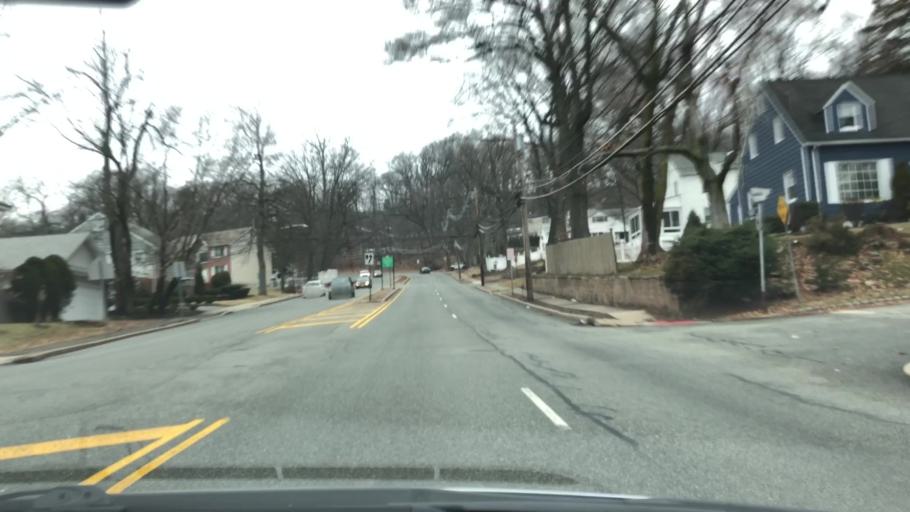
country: US
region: New Jersey
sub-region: Essex County
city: Orange
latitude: 40.7772
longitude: -74.2535
